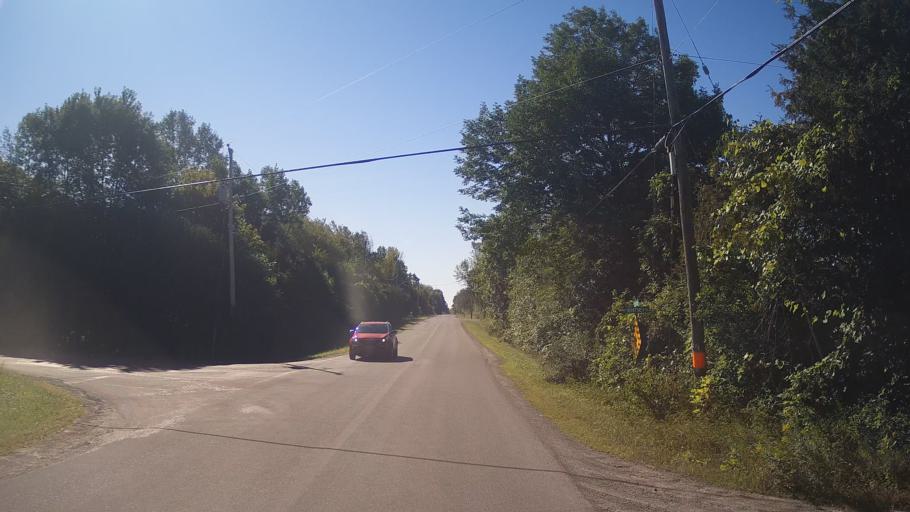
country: CA
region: Ontario
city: Prescott
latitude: 44.9993
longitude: -75.5971
